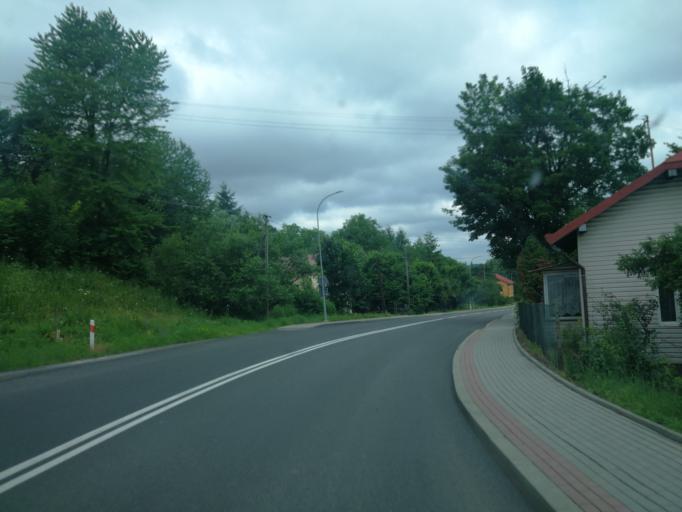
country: PL
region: Subcarpathian Voivodeship
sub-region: Powiat leski
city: Lesko
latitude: 49.4643
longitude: 22.3387
